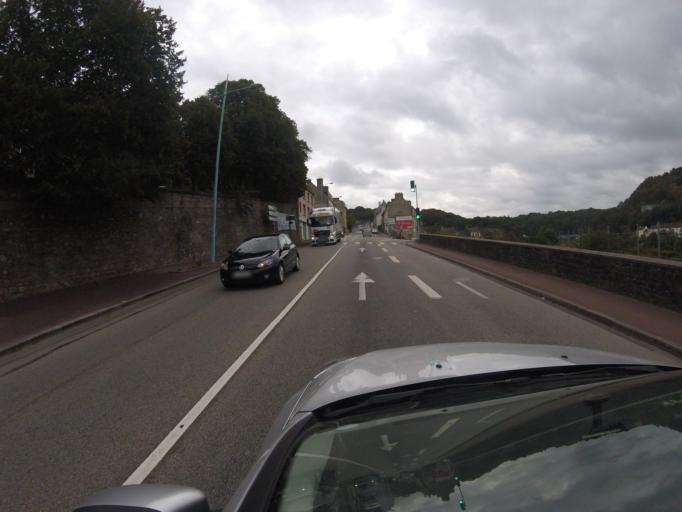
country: FR
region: Lower Normandy
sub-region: Departement de la Manche
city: Cherbourg-Octeville
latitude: 49.6260
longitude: -1.6171
